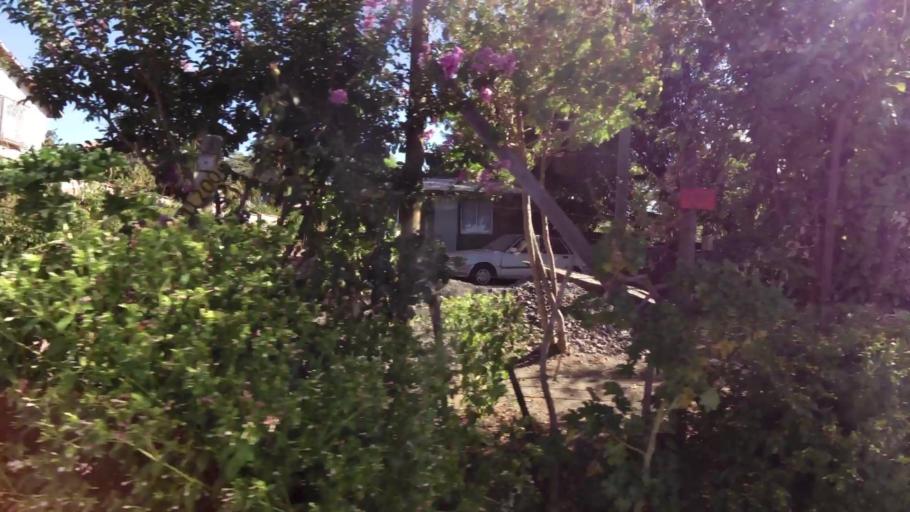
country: CL
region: Maule
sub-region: Provincia de Talca
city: Talca
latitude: -35.4026
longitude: -71.6075
